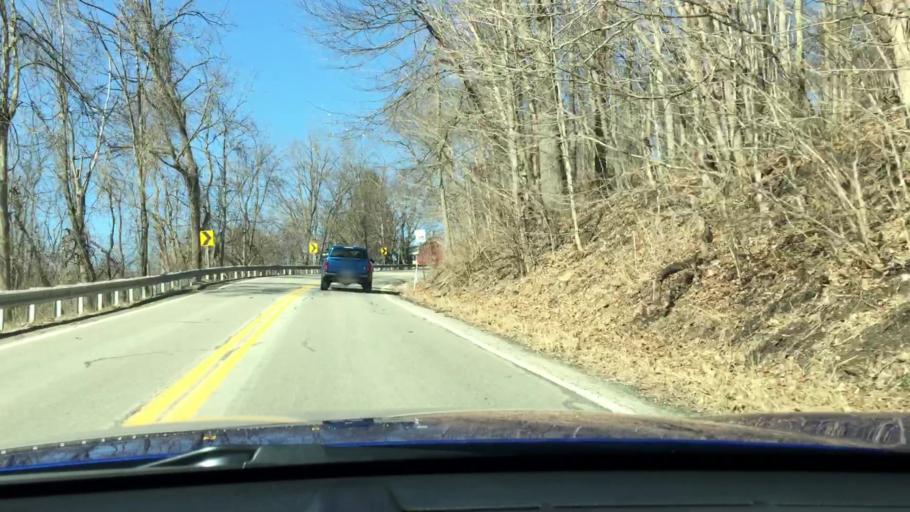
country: US
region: Pennsylvania
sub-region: Washington County
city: Cecil-Bishop
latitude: 40.3002
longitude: -80.1529
